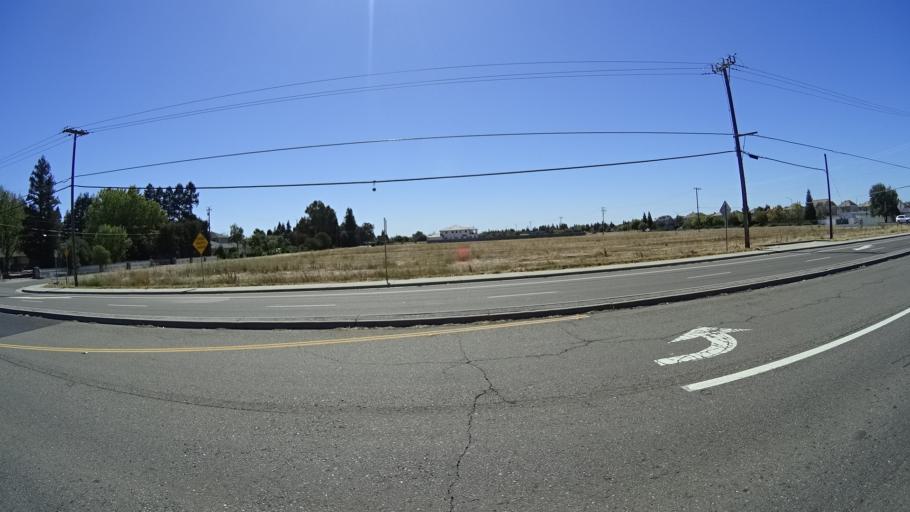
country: US
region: California
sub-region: Sacramento County
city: Elk Grove
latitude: 38.4381
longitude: -121.3706
